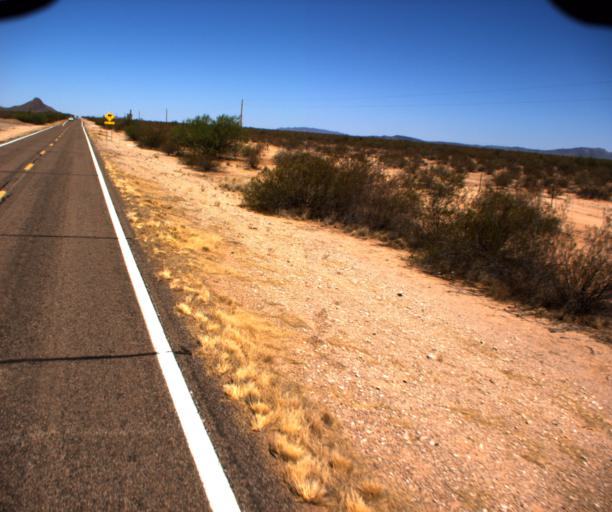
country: US
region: Arizona
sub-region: Pima County
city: Ajo
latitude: 32.1981
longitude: -112.4769
